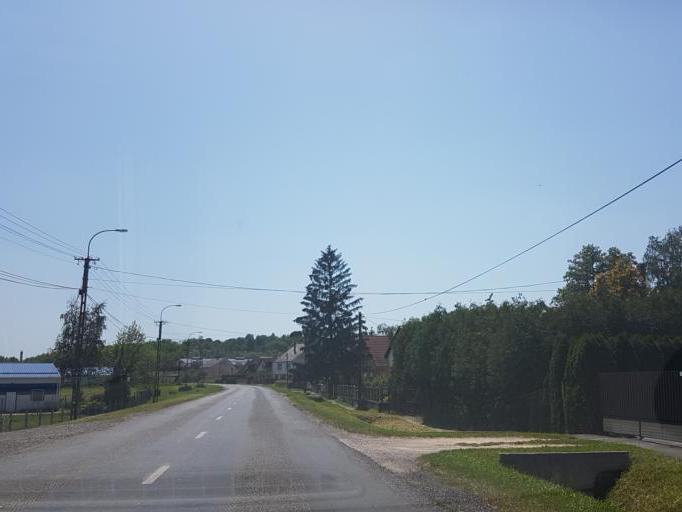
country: HU
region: Zala
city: Zalaegerszeg
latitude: 46.8476
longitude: 16.7730
